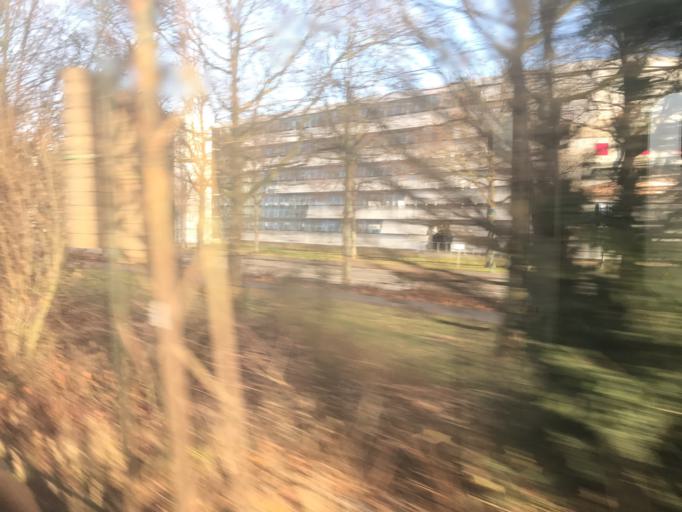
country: DE
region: North Rhine-Westphalia
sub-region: Regierungsbezirk Koln
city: Bonn
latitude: 50.7062
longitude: 7.1264
